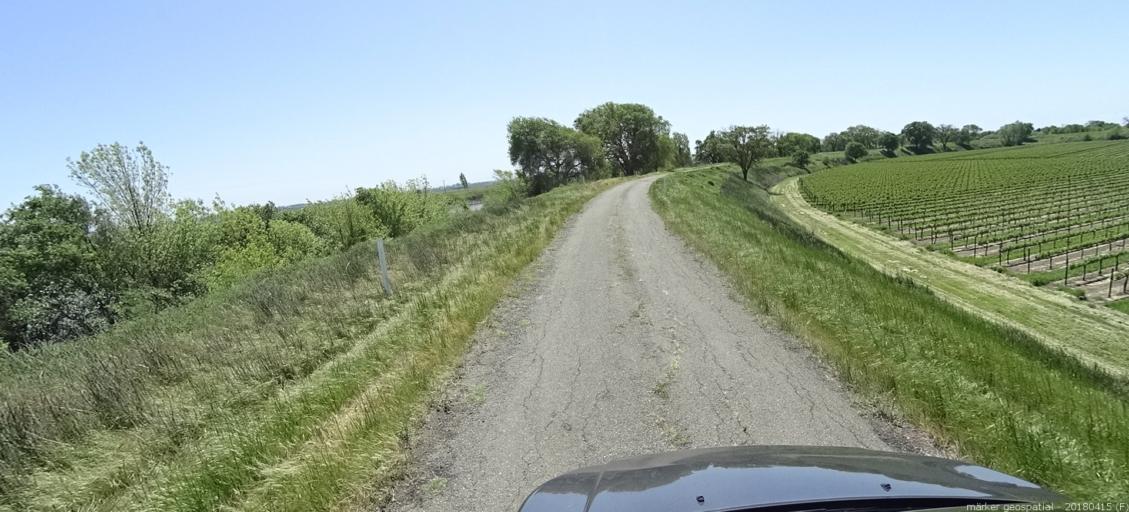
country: US
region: California
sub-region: Sacramento County
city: Walnut Grove
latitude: 38.2579
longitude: -121.5952
